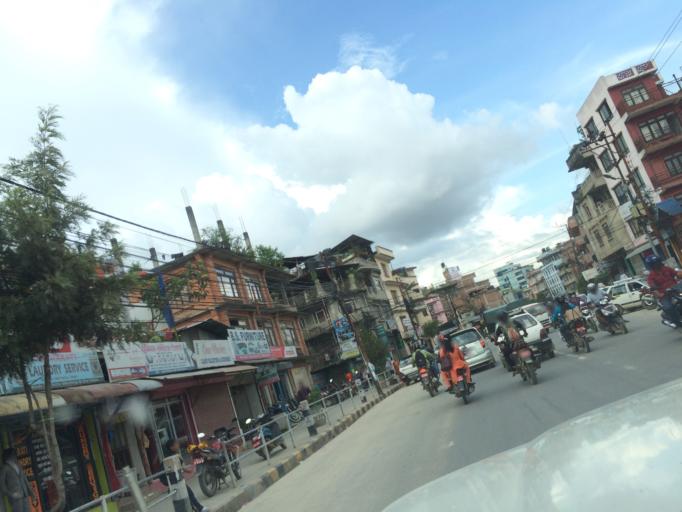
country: NP
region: Central Region
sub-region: Bagmati Zone
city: Kathmandu
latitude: 27.7175
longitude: 85.3056
